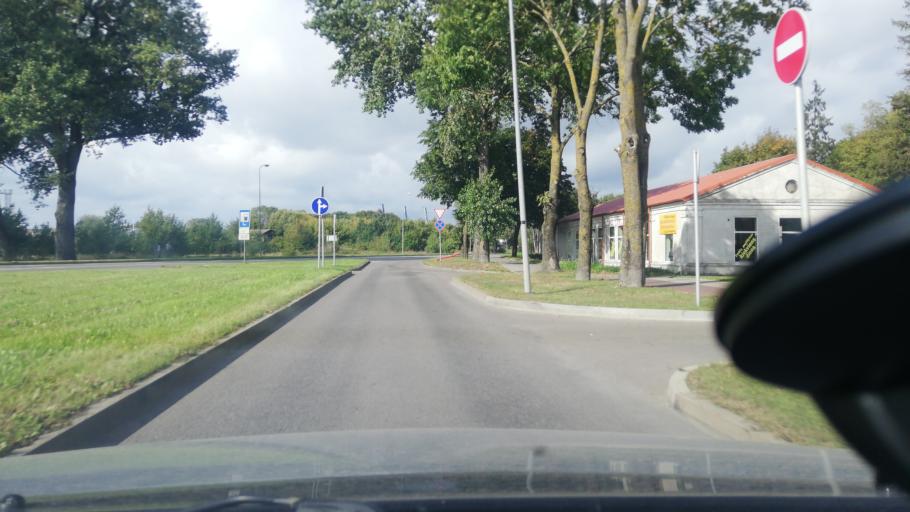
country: LT
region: Klaipedos apskritis
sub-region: Klaipeda
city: Klaipeda
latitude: 55.6668
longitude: 21.1627
